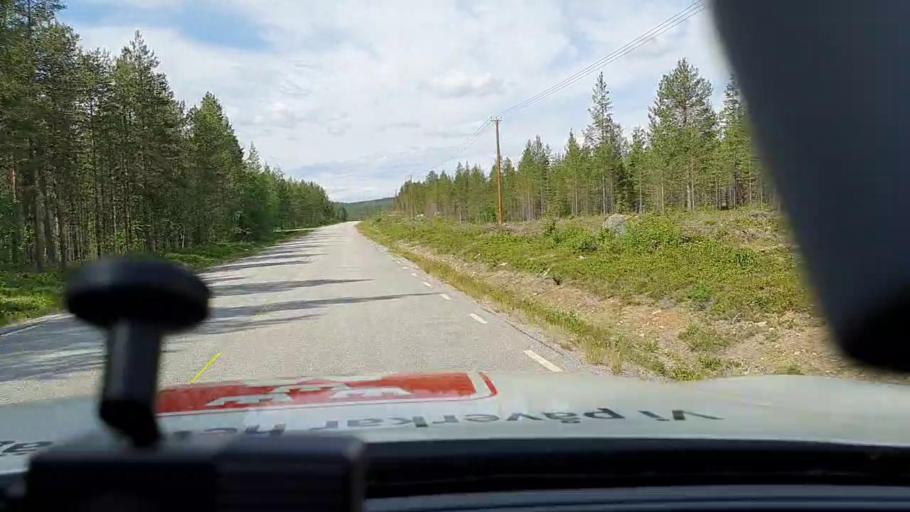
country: SE
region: Norrbotten
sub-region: Jokkmokks Kommun
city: Jokkmokk
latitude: 66.6234
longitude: 19.6789
